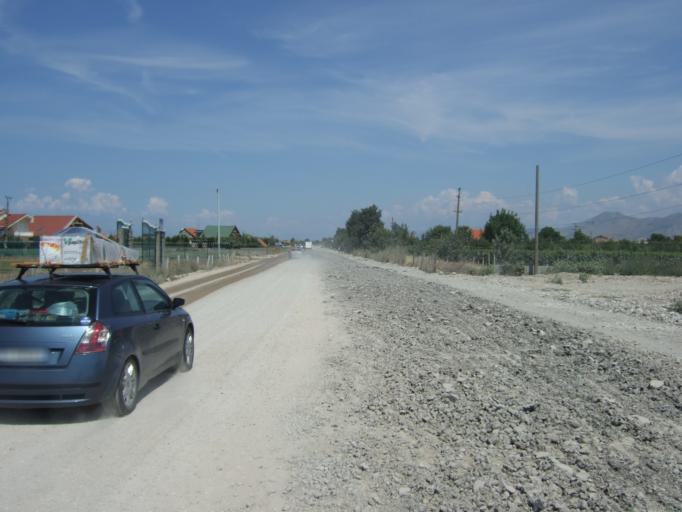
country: AL
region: Shkoder
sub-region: Rrethi i Shkodres
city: Shkoder
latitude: 42.1088
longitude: 19.5022
